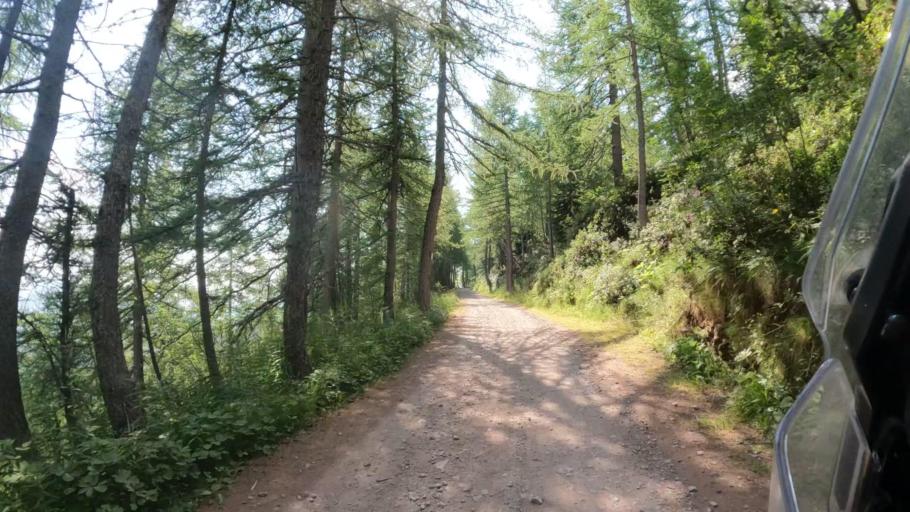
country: IT
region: Piedmont
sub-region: Provincia di Cuneo
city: Briga Alta
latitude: 44.1075
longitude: 7.7062
